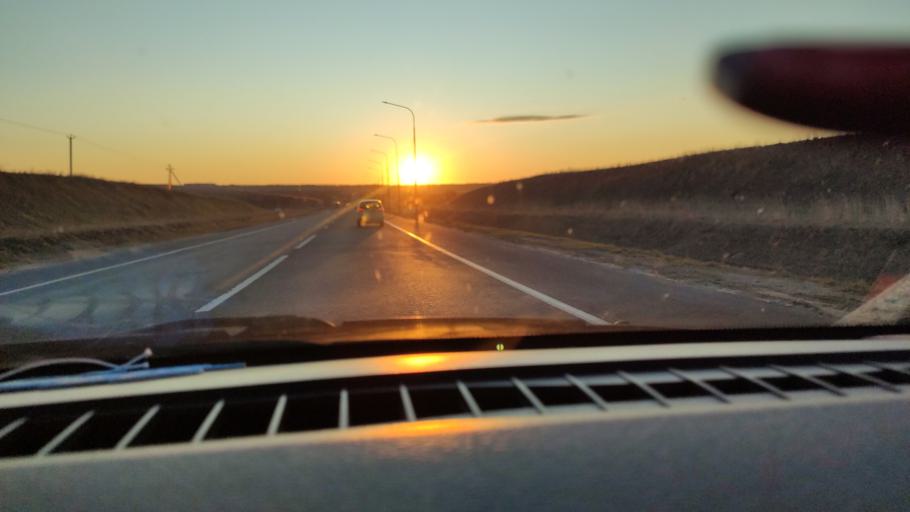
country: RU
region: Saratov
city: Yelshanka
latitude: 51.8238
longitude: 46.3821
